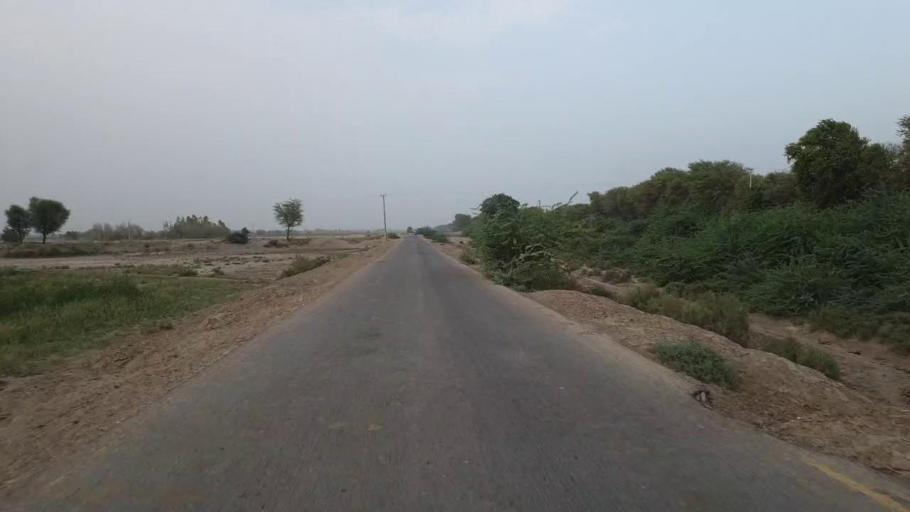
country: PK
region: Sindh
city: Daur
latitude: 26.4376
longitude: 68.2736
